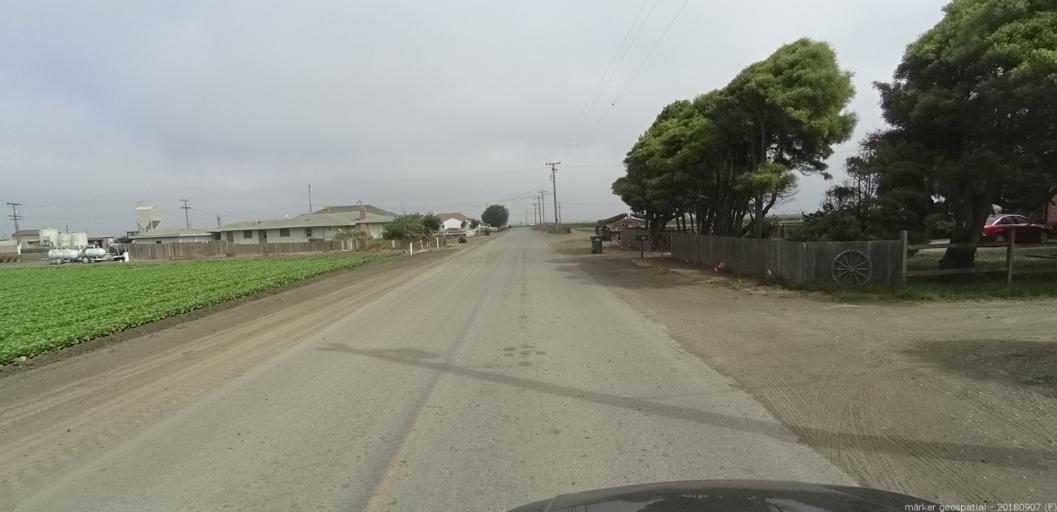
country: US
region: California
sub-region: Monterey County
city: Boronda
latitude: 36.6899
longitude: -121.7078
